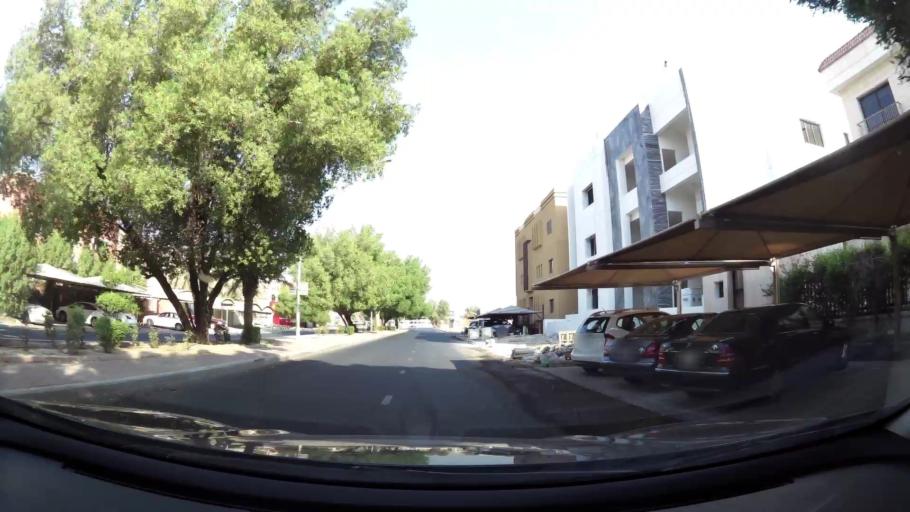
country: KW
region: Muhafazat Hawalli
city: Hawalli
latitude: 29.3234
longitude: 48.0381
